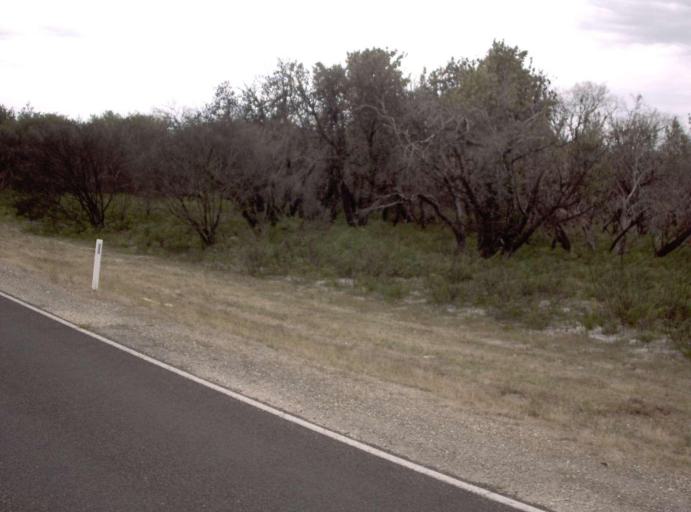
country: AU
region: Victoria
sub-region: East Gippsland
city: Bairnsdale
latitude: -38.0837
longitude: 147.5287
